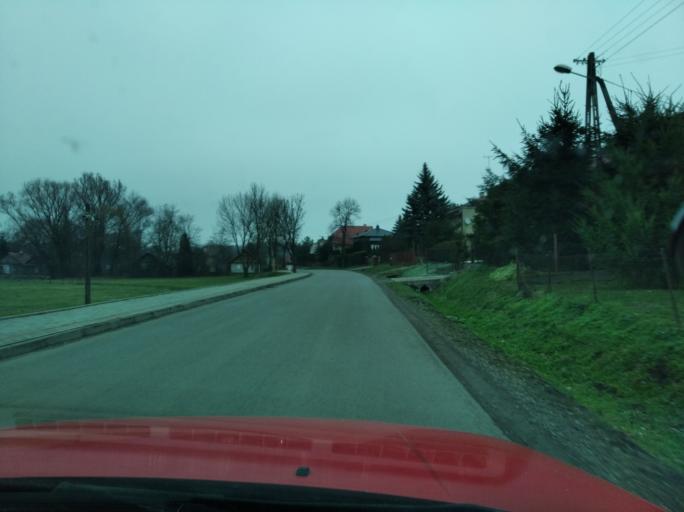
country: PL
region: Subcarpathian Voivodeship
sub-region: Powiat jaroslawski
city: Pawlosiow
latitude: 50.0003
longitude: 22.6500
